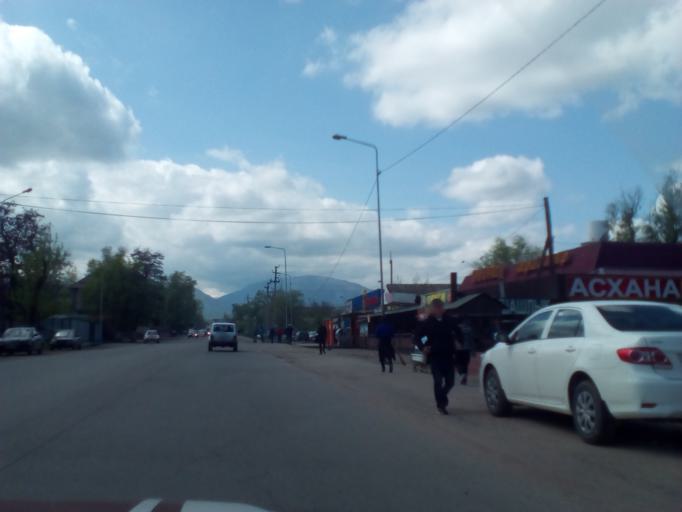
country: KZ
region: Almaty Oblysy
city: Burunday
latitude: 43.2114
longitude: 76.6417
